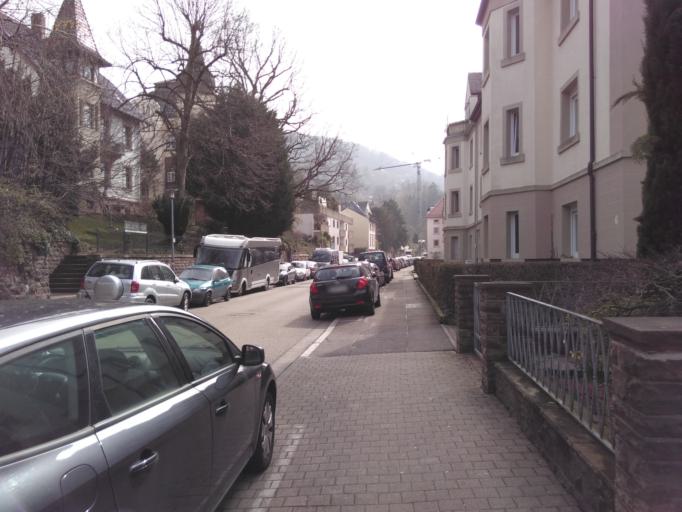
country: DE
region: Baden-Wuerttemberg
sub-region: Karlsruhe Region
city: Ettlingen
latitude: 48.9422
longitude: 8.4133
